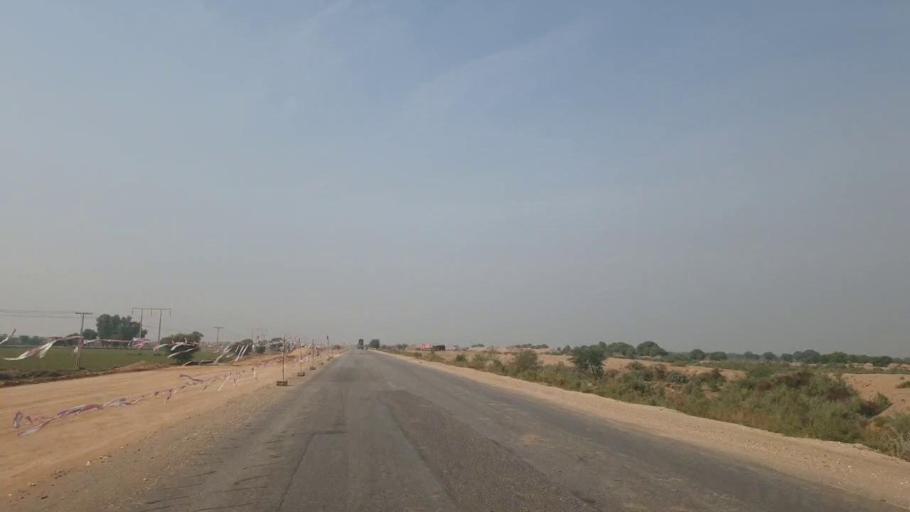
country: PK
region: Sindh
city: Sann
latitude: 26.1388
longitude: 68.0407
